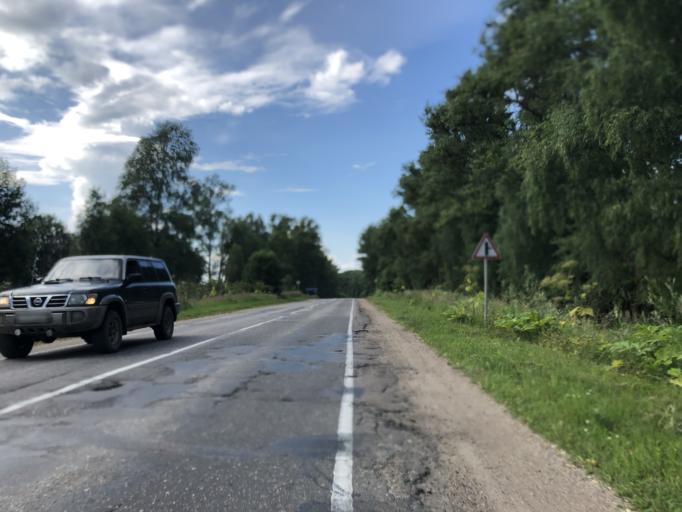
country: RU
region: Tverskaya
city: Rzhev
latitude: 56.2643
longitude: 34.2516
